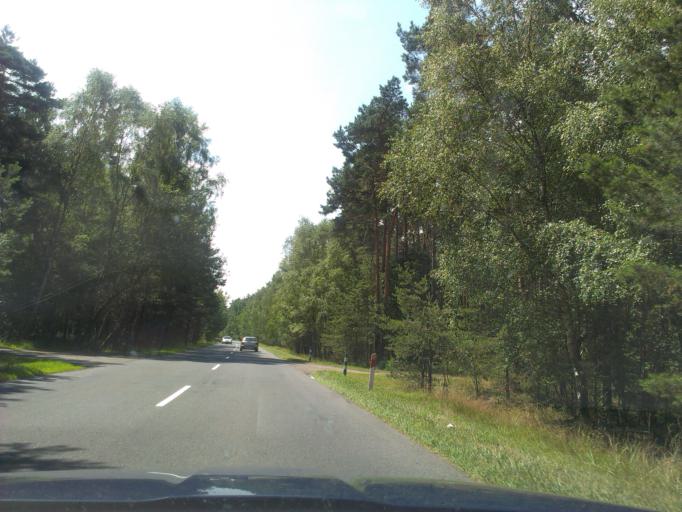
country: PL
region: West Pomeranian Voivodeship
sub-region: Swinoujscie
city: Swinoujscie
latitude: 53.8833
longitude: 14.3183
